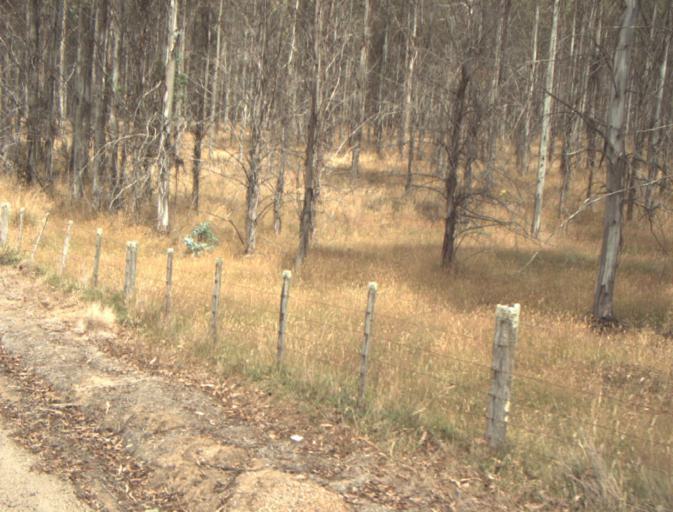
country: AU
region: Tasmania
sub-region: Dorset
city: Scottsdale
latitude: -41.4141
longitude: 147.5254
